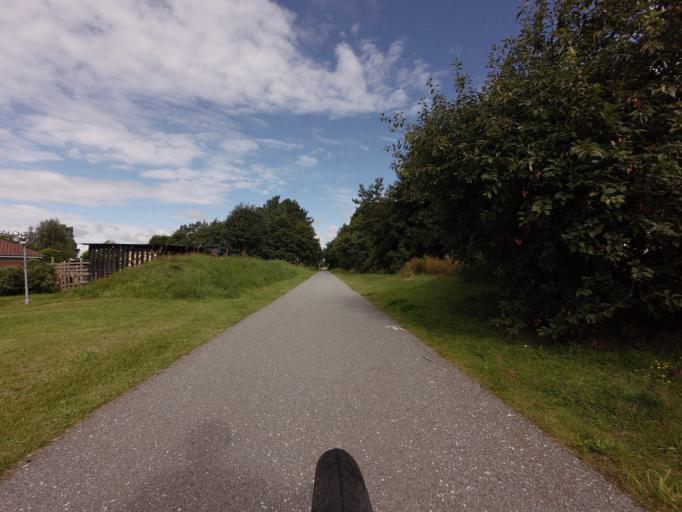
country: DK
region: Central Jutland
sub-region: Norddjurs Kommune
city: Auning
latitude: 56.4329
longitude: 10.3746
